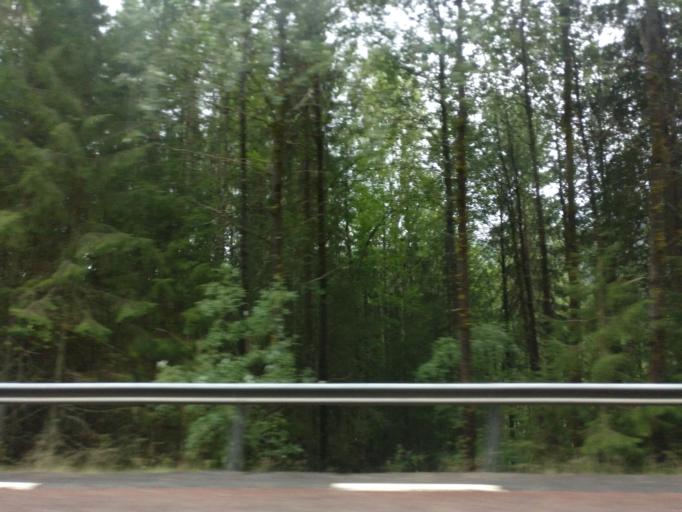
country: SE
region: Vaermland
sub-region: Torsby Kommun
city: Torsby
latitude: 60.7007
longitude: 12.9097
